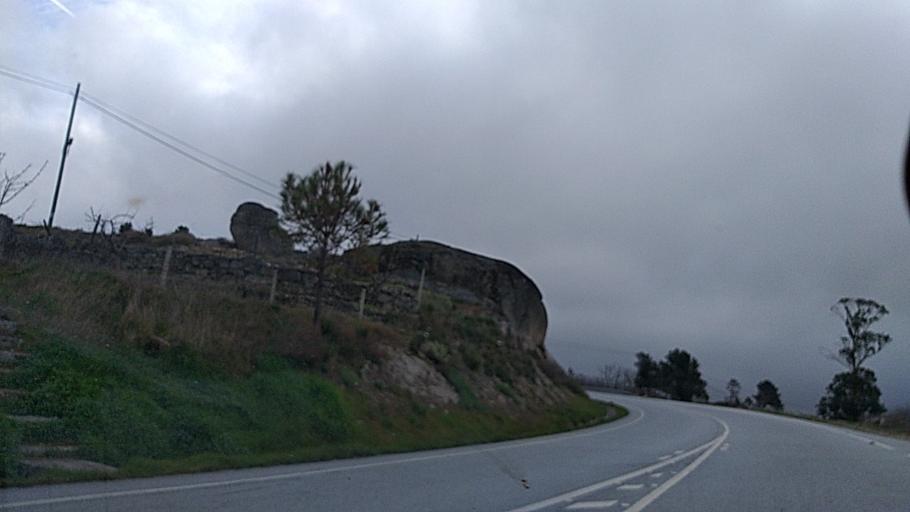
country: PT
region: Guarda
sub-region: Fornos de Algodres
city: Fornos de Algodres
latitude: 40.6589
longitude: -7.4837
